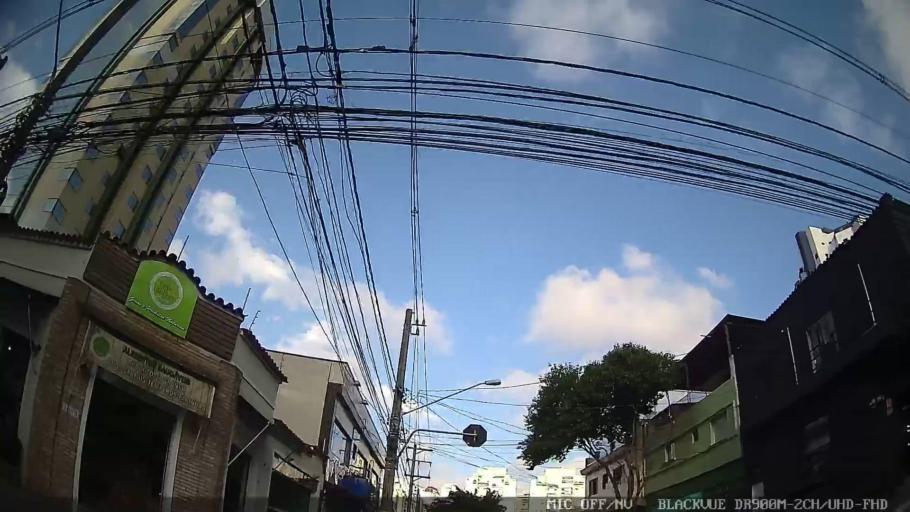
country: BR
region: Sao Paulo
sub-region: Sao Caetano Do Sul
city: Sao Caetano do Sul
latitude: -23.5463
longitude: -46.5581
